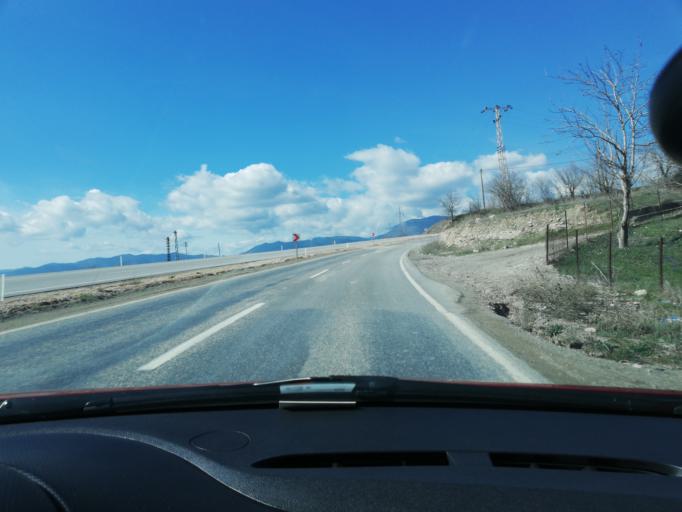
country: TR
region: Karabuk
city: Safranbolu
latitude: 41.2183
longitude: 32.7288
